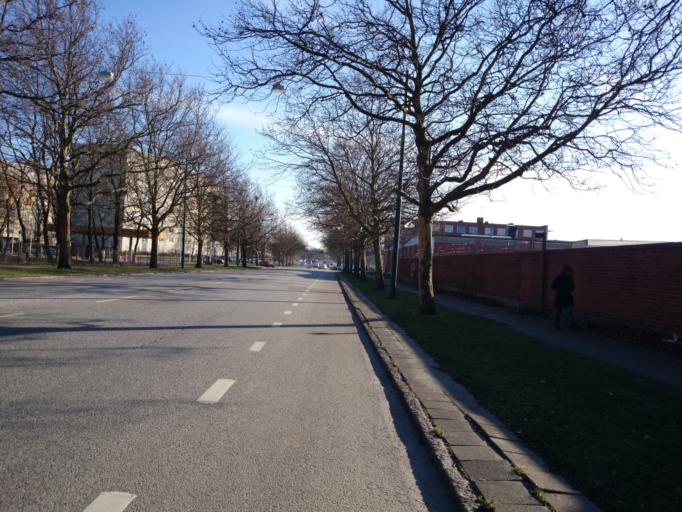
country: SE
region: Skane
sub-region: Malmo
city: Malmoe
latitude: 55.5913
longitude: 13.0376
